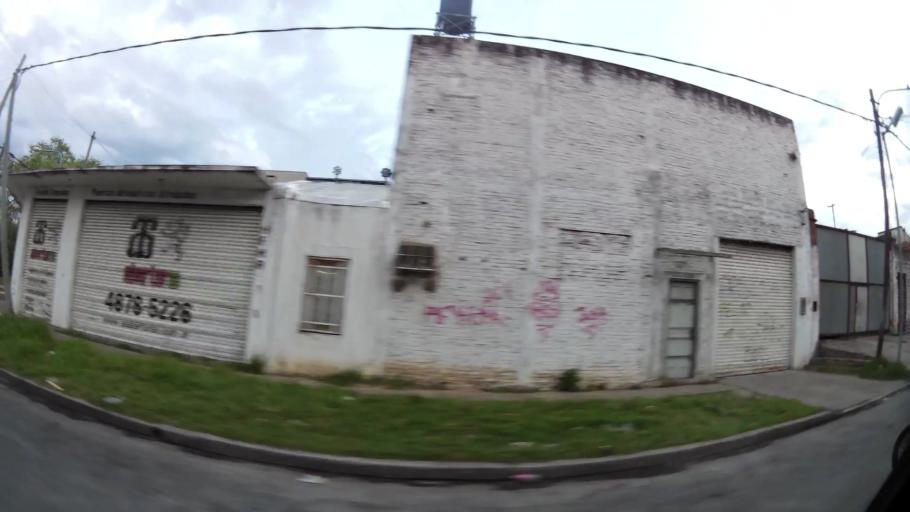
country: AR
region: Buenos Aires
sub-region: Partido de Quilmes
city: Quilmes
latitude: -34.7425
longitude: -58.2453
